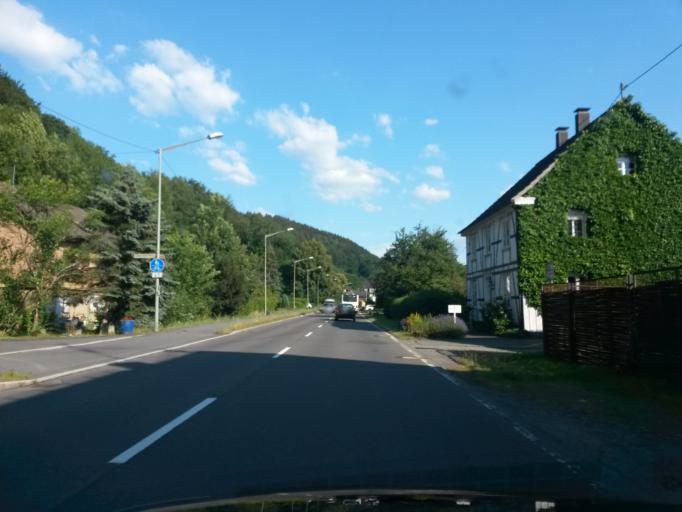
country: DE
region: North Rhine-Westphalia
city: Wiehl
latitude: 50.9921
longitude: 7.5052
